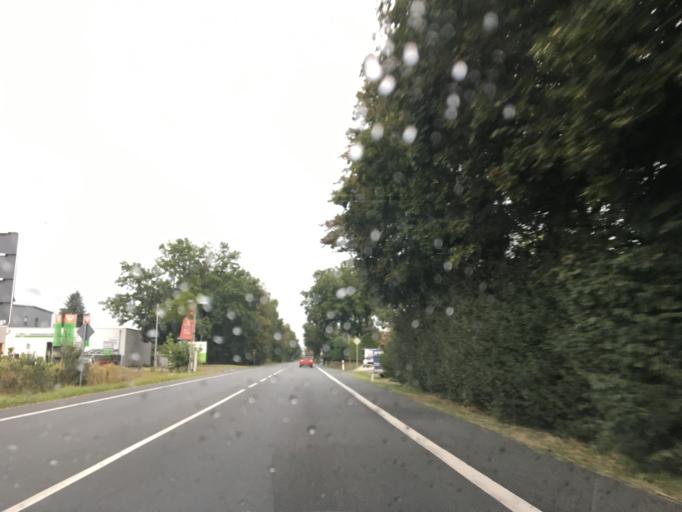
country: DE
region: Hesse
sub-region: Regierungsbezirk Darmstadt
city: Egelsbach
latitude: 49.9644
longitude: 8.6751
